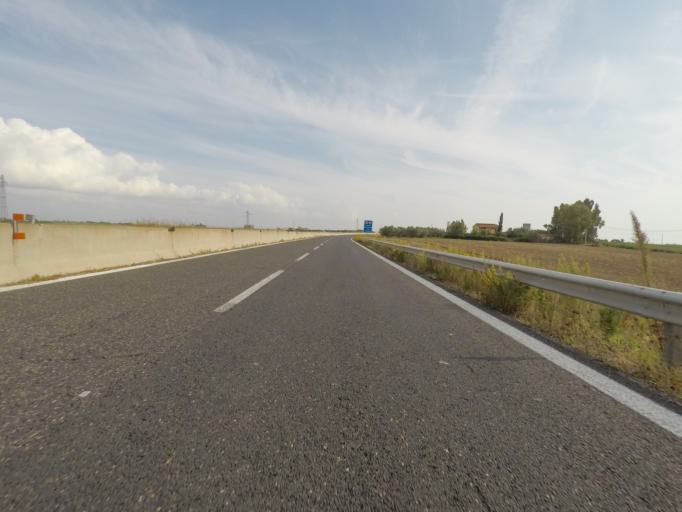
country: IT
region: Latium
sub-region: Provincia di Viterbo
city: Montalto di Castro
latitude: 42.3632
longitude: 11.5814
